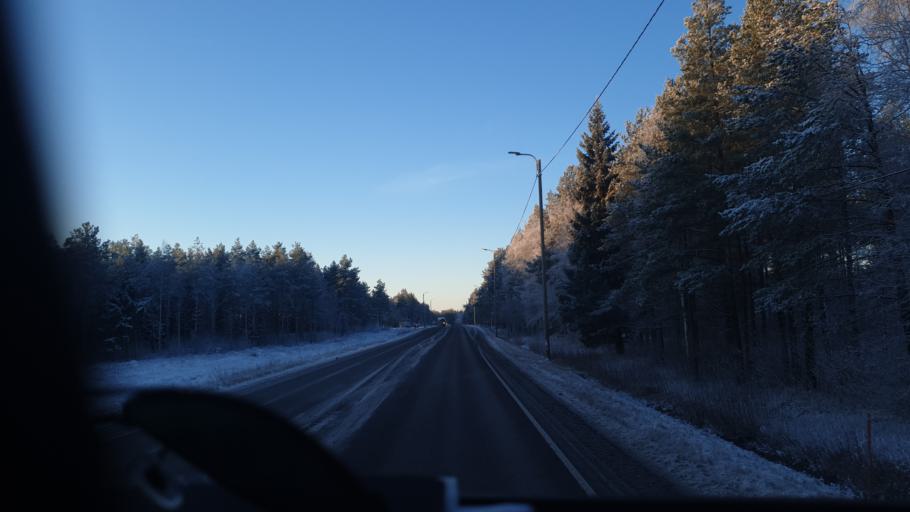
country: FI
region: Northern Ostrobothnia
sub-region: Ylivieska
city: Kalajoki
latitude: 64.2449
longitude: 23.8667
